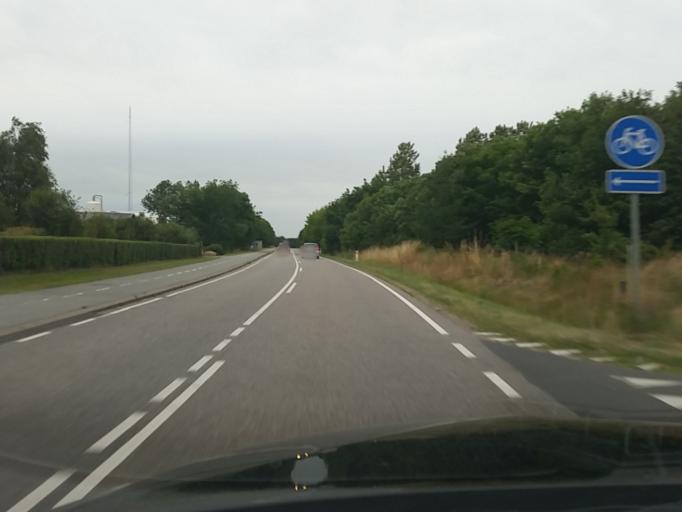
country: DK
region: South Denmark
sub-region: Billund Kommune
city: Grindsted
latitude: 55.6566
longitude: 8.8056
